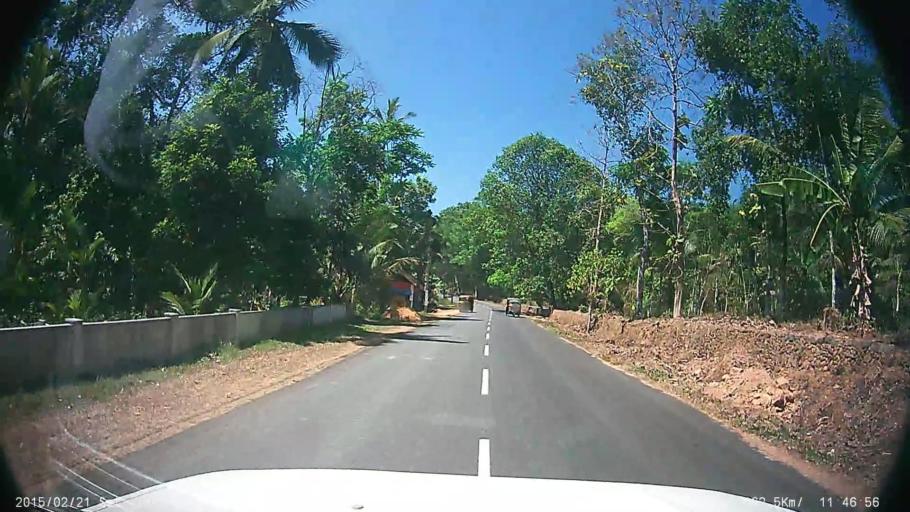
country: IN
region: Kerala
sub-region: Kottayam
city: Lalam
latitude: 9.7762
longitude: 76.7192
